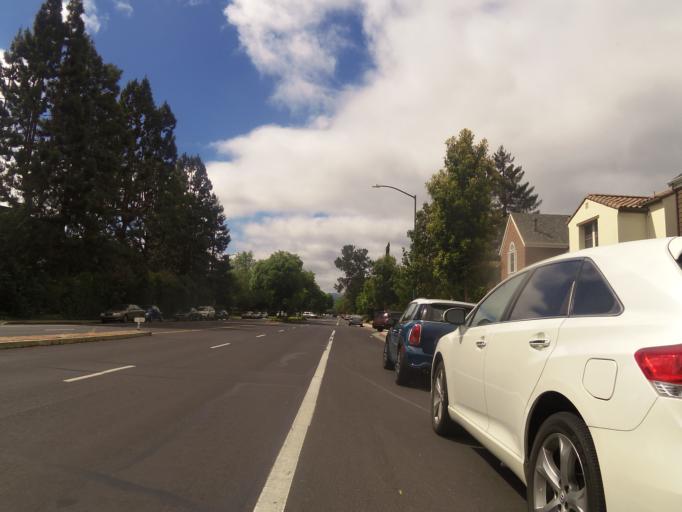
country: US
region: California
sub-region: Santa Clara County
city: Mountain View
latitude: 37.3840
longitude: -122.0871
